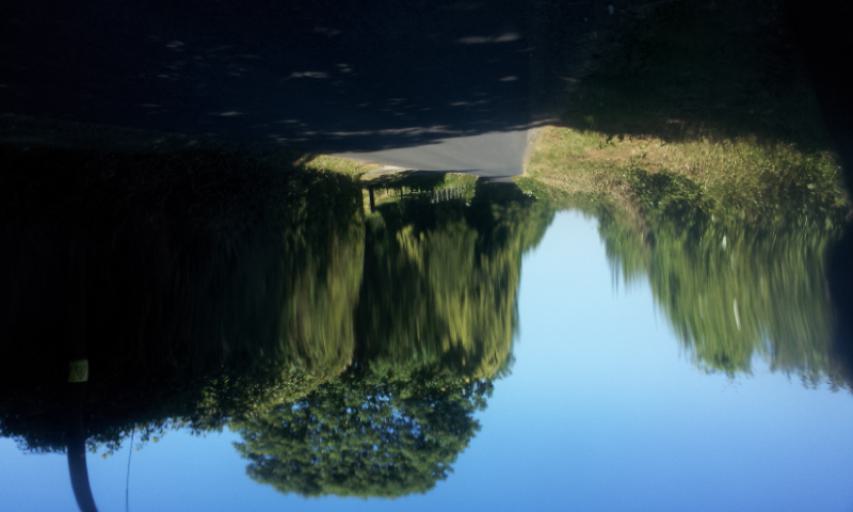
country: GB
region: England
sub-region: Kent
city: Sittingbourne
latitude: 51.3046
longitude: 0.7378
